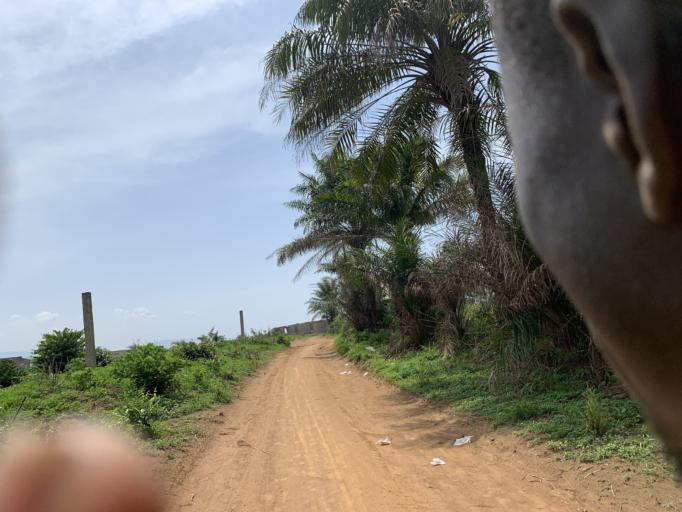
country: SL
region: Western Area
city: Waterloo
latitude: 8.3545
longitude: -13.0445
